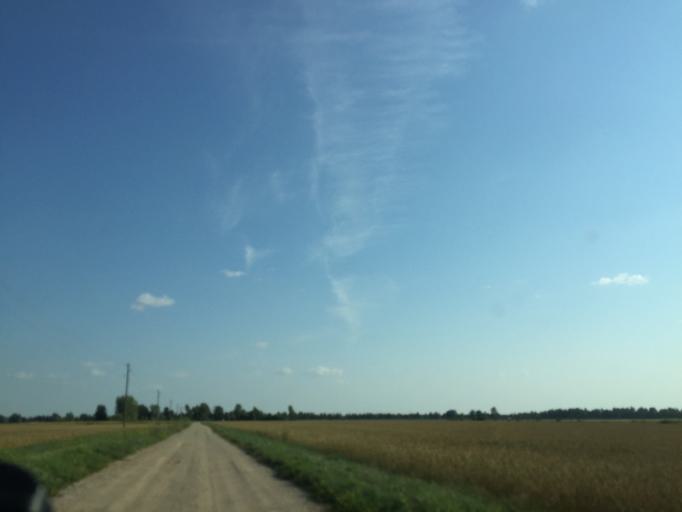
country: LV
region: Jelgava
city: Jelgava
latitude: 56.4597
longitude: 23.6806
